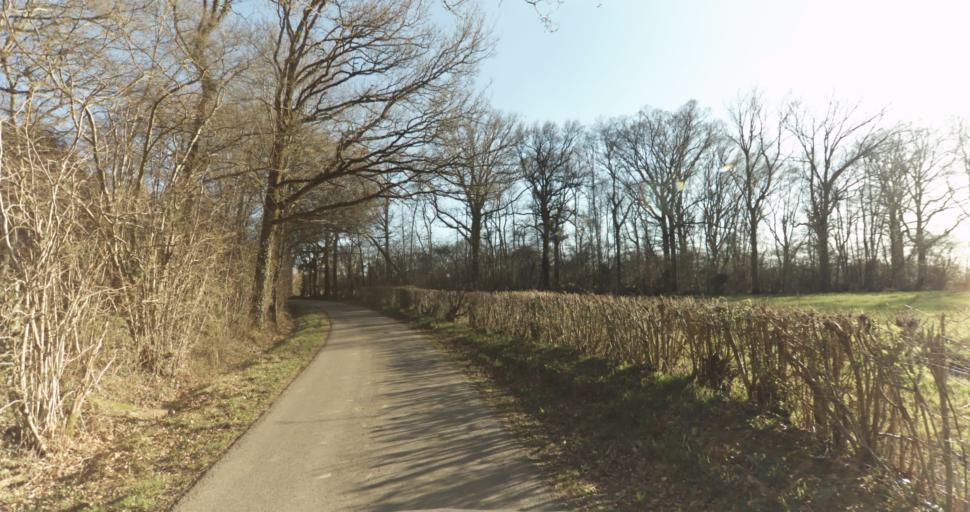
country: FR
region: Lower Normandy
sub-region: Departement du Calvados
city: Livarot
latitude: 48.9879
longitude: 0.0847
